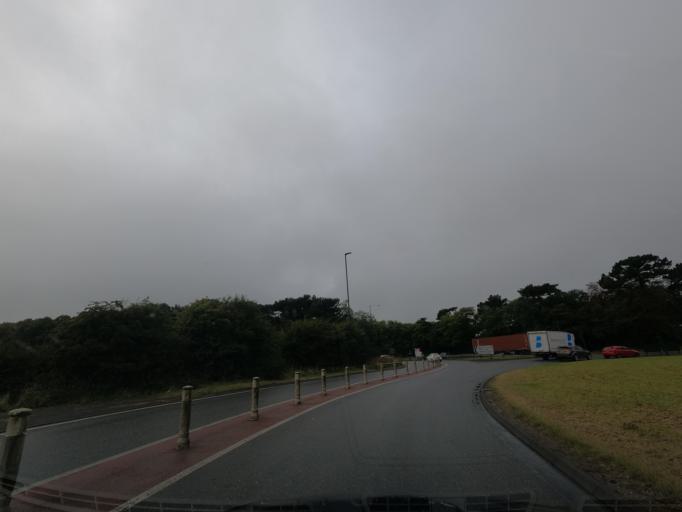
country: GB
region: England
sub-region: Redcar and Cleveland
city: Redcar
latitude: 54.5826
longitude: -1.0880
